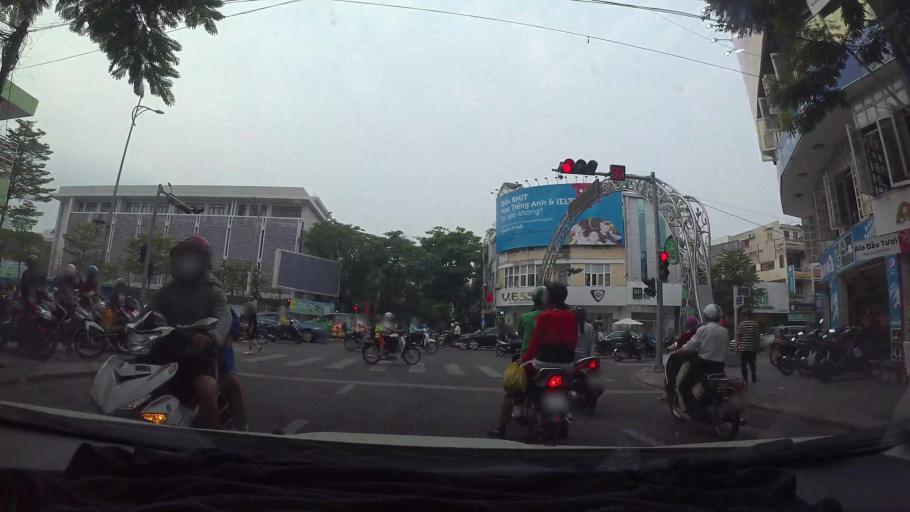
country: VN
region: Da Nang
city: Da Nang
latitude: 16.0713
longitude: 108.2211
